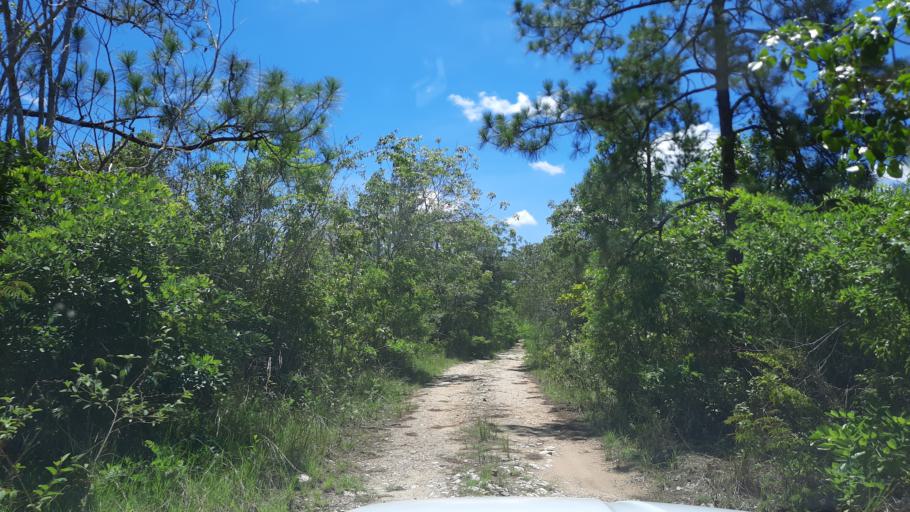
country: BZ
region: Cayo
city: Belmopan
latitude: 17.3557
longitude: -88.5446
